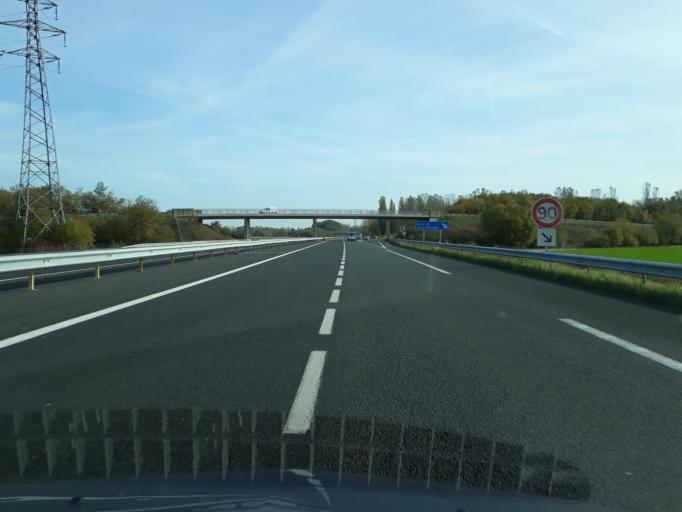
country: FR
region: Champagne-Ardenne
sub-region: Departement de l'Aube
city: Saint-Pouange
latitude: 48.2344
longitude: 4.0311
